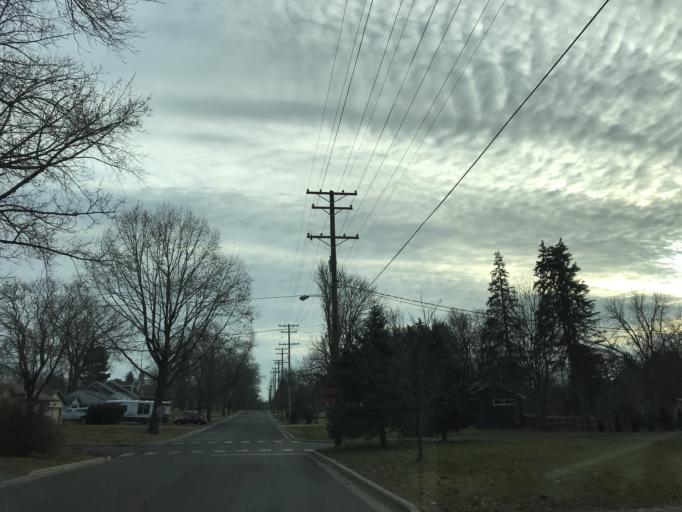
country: US
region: Wisconsin
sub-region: Dane County
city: Monona
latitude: 43.0661
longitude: -89.3335
